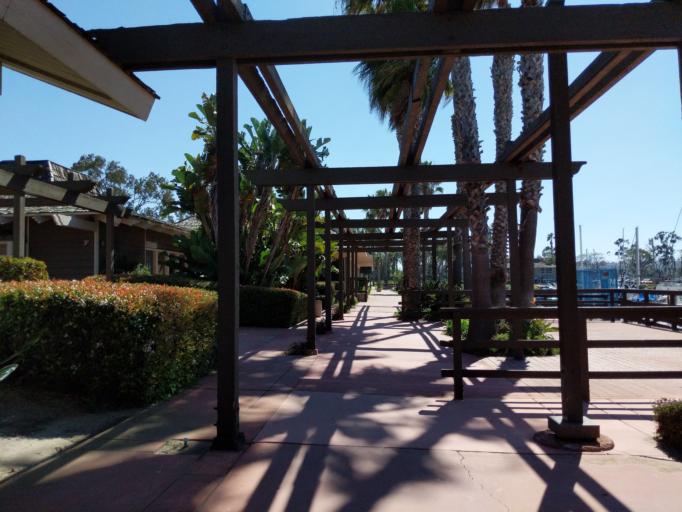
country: US
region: California
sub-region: San Diego County
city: San Diego
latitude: 32.7617
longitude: -117.2343
